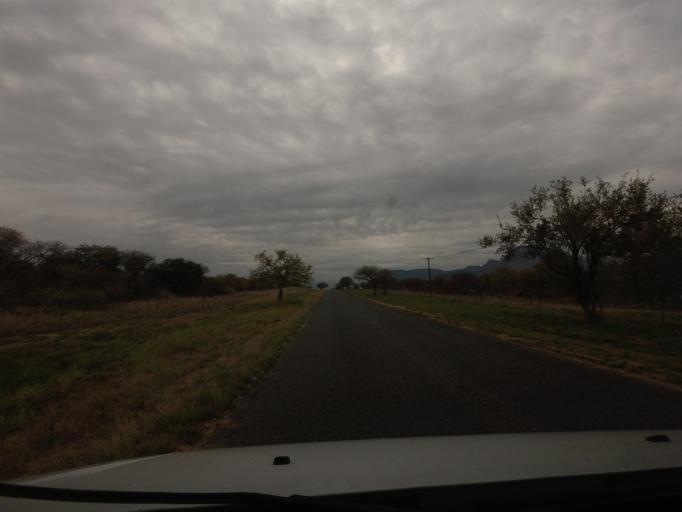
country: ZA
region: Limpopo
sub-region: Mopani District Municipality
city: Hoedspruit
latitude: -24.4591
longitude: 30.8682
